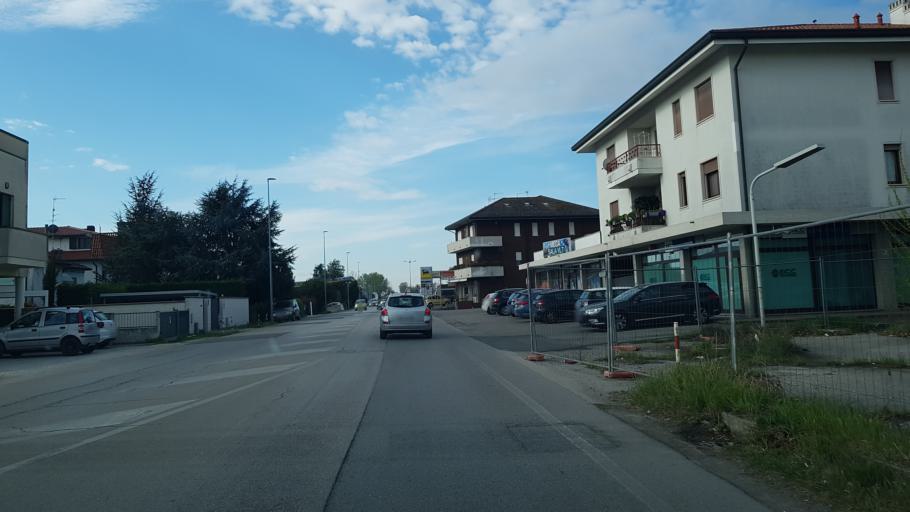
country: IT
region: Veneto
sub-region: Provincia di Rovigo
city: Rovigo
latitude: 45.0603
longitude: 11.7923
